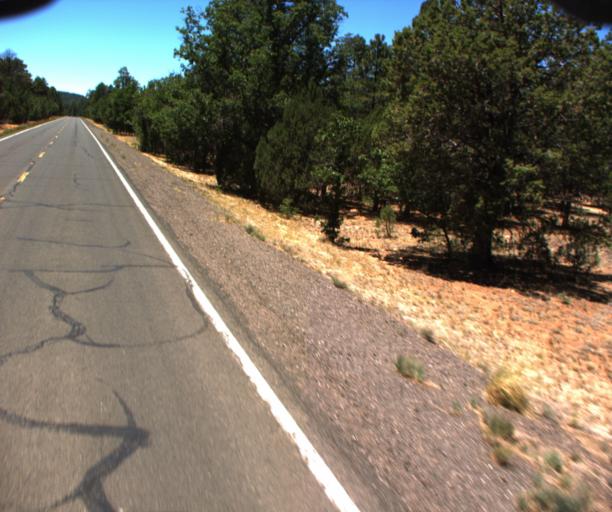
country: US
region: Arizona
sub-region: Gila County
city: Pine
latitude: 34.6179
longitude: -111.1764
